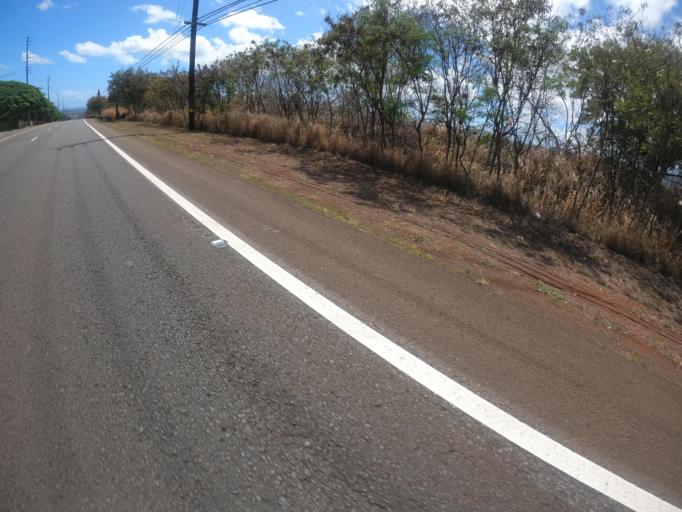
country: US
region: Hawaii
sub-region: Honolulu County
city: Village Park
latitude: 21.3920
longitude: -158.0361
